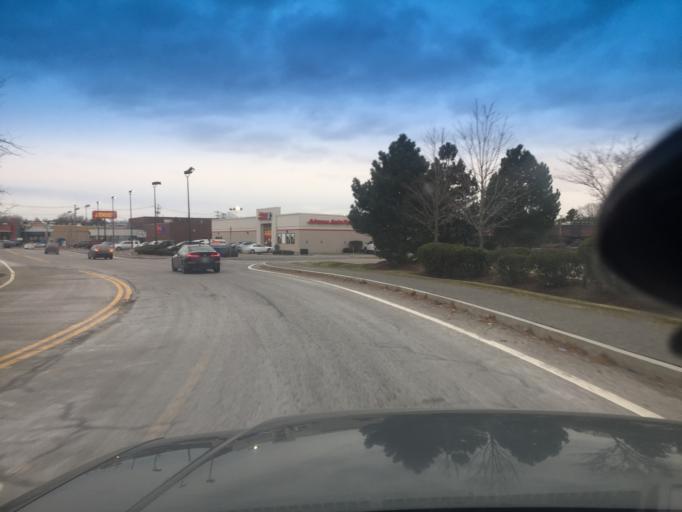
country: US
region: Massachusetts
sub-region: Norfolk County
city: Norwood
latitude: 42.1803
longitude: -71.1907
